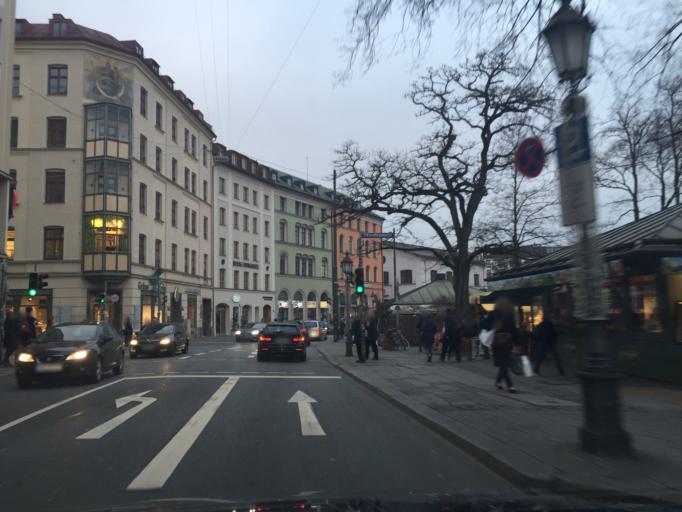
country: DE
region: Bavaria
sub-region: Upper Bavaria
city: Munich
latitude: 48.1345
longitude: 11.5769
